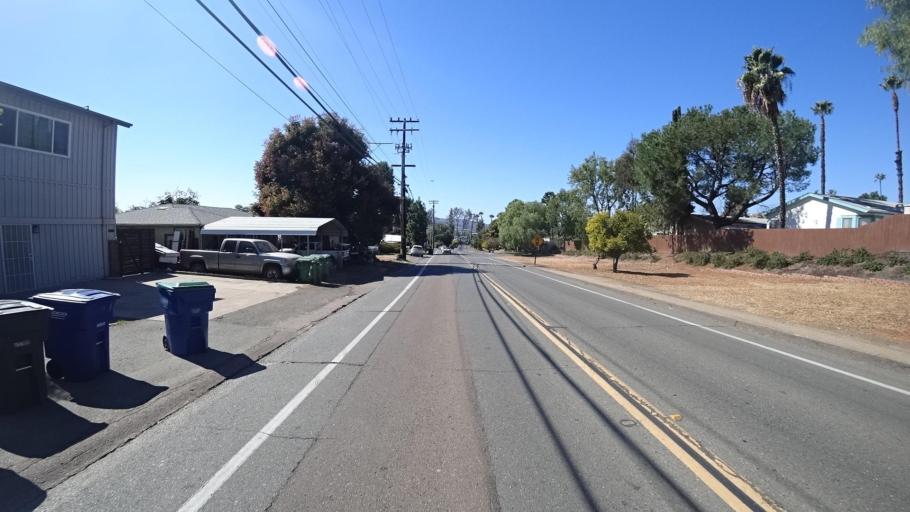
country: US
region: California
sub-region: San Diego County
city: Winter Gardens
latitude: 32.8213
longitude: -116.9429
